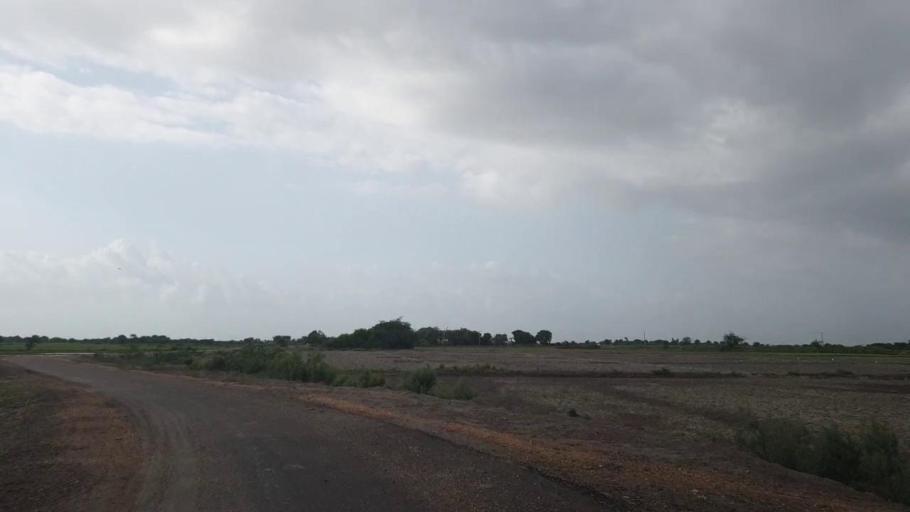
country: PK
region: Sindh
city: Kadhan
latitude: 24.5982
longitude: 69.0569
